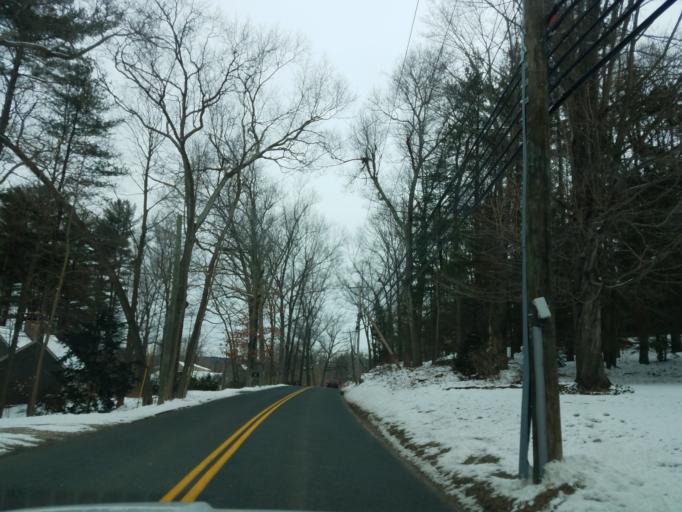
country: US
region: Connecticut
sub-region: Hartford County
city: Collinsville
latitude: 41.7686
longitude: -72.8984
